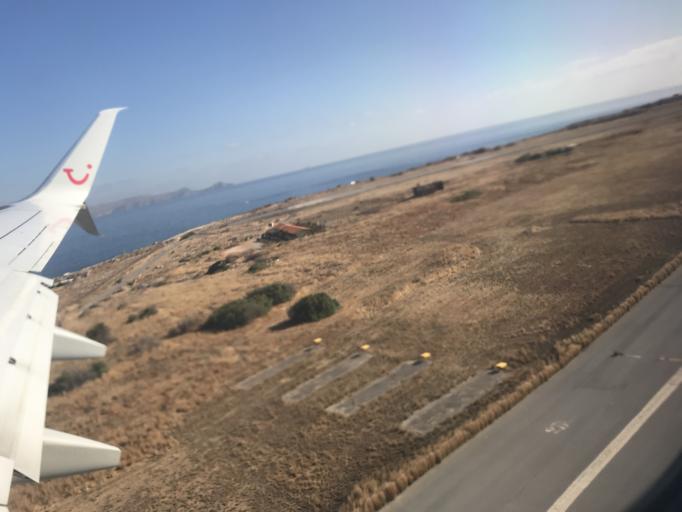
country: GR
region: Crete
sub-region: Nomos Irakleiou
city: Nea Alikarnassos
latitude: 35.3409
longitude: 25.1702
